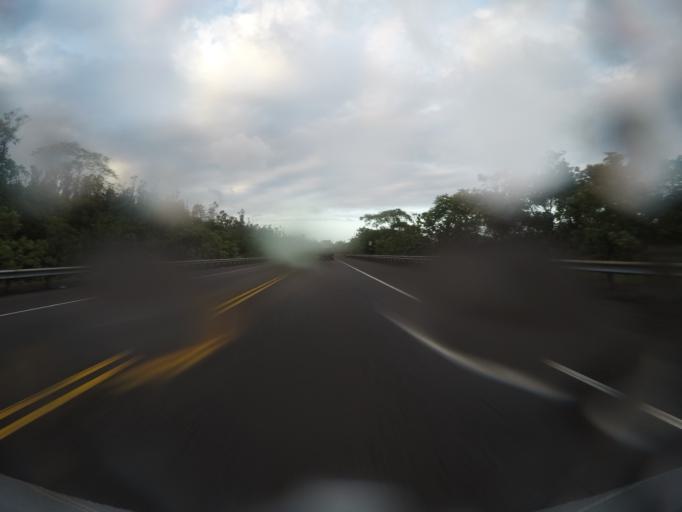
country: US
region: Hawaii
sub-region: Hawaii County
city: Hilo
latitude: 19.6890
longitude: -155.1163
